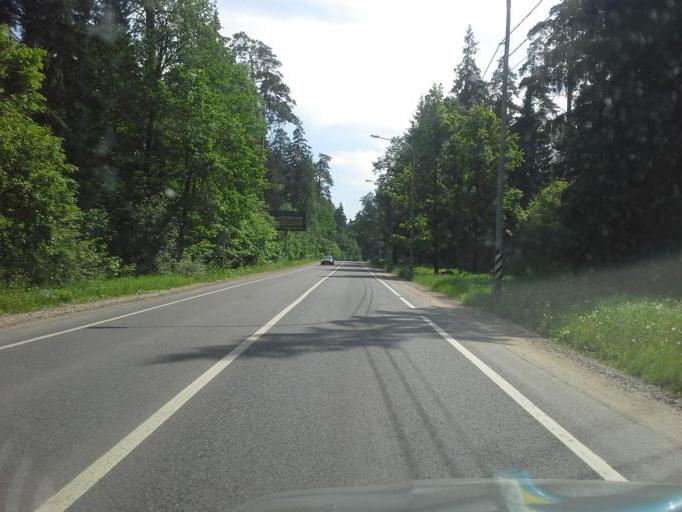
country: RU
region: Moskovskaya
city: Gorki Vtoryye
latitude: 55.7120
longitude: 37.1652
